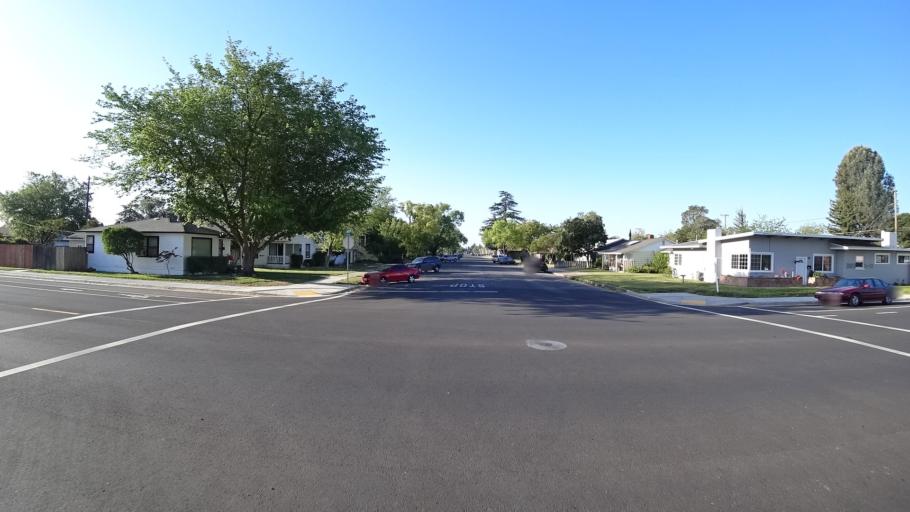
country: US
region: California
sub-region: Glenn County
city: Orland
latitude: 39.7496
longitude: -122.1889
